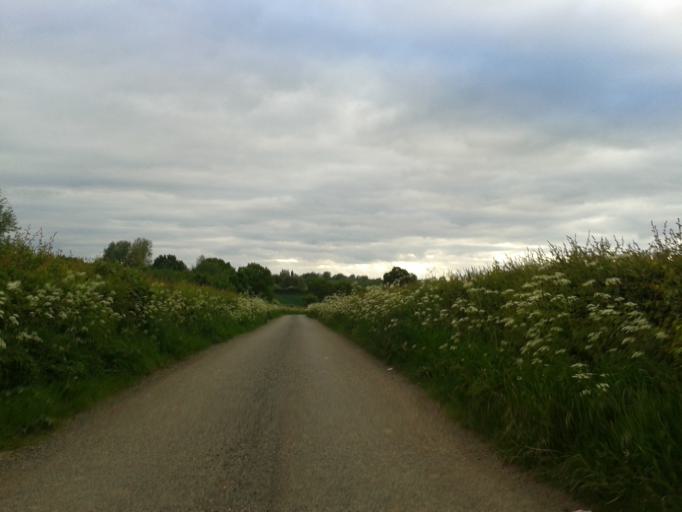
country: GB
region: England
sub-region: Leicestershire
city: Earl Shilton
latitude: 52.5513
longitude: -1.3317
